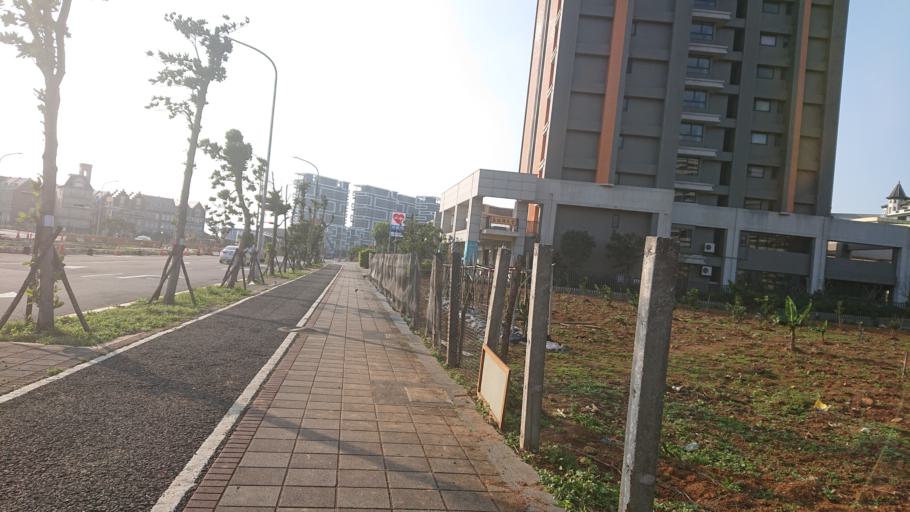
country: TW
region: Taipei
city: Taipei
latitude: 25.1911
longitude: 121.4283
